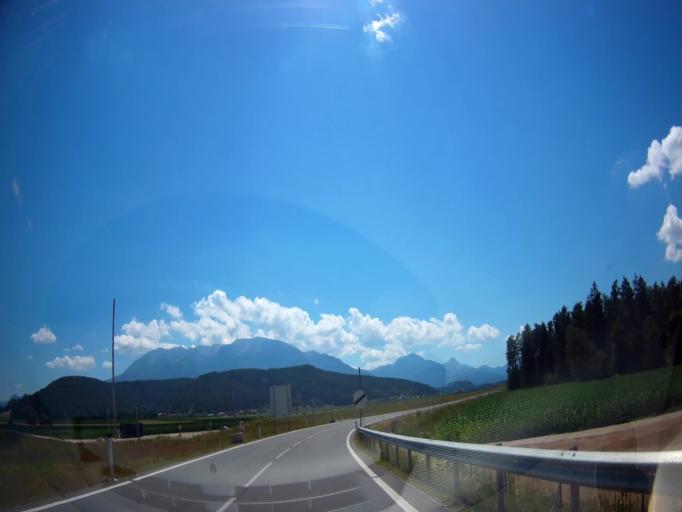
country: AT
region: Carinthia
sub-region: Politischer Bezirk Volkermarkt
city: Bleiburg/Pliberk
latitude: 46.6094
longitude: 14.7813
